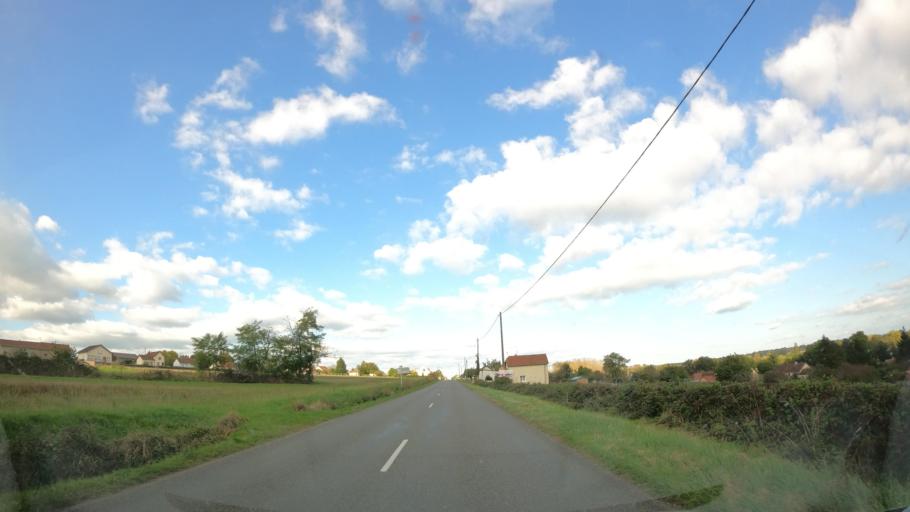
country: FR
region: Auvergne
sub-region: Departement de l'Allier
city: Dompierre-sur-Besbre
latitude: 46.5096
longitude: 3.6731
